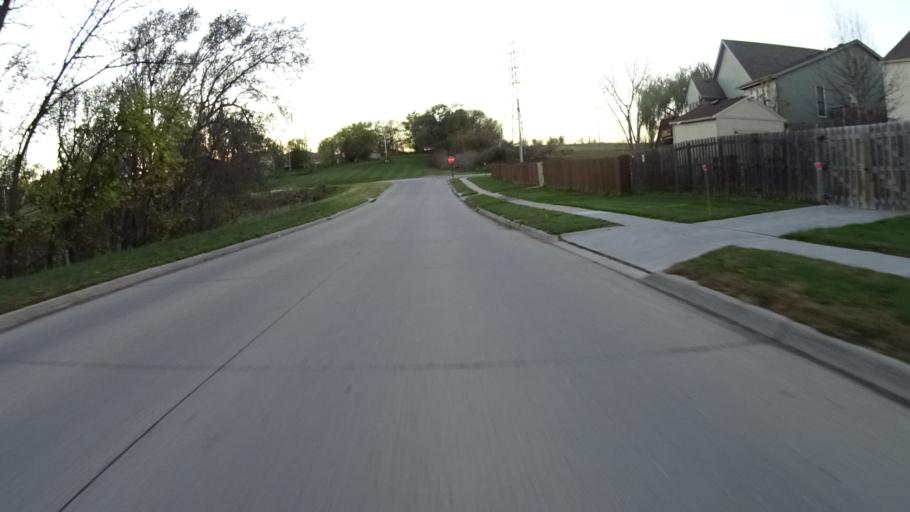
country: US
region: Nebraska
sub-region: Sarpy County
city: Offutt Air Force Base
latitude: 41.1619
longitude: -95.9550
